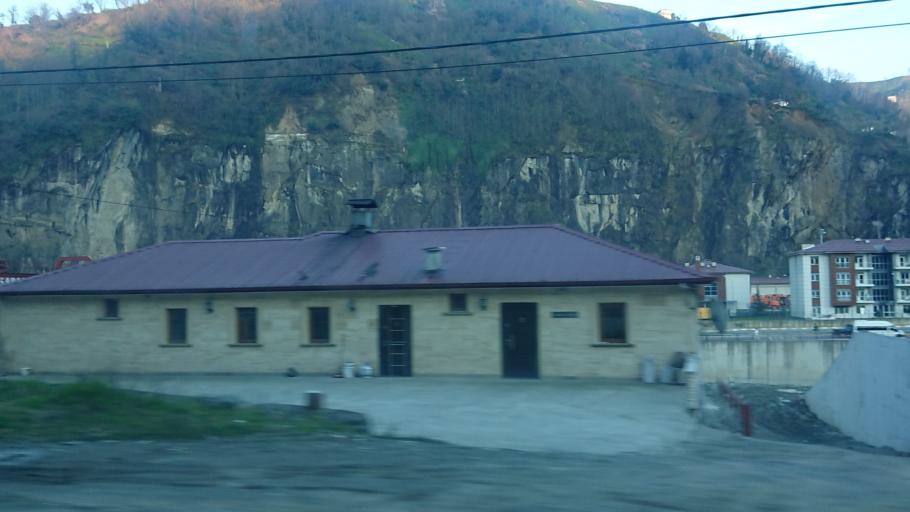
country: TR
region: Rize
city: Gundogdu
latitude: 41.0288
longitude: 40.5815
